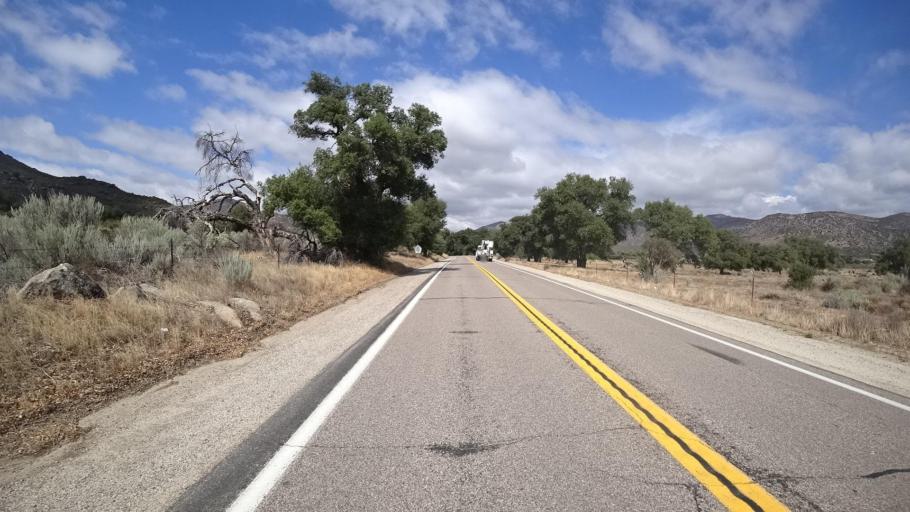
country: US
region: California
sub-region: San Diego County
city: Pine Valley
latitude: 32.7366
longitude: -116.4939
